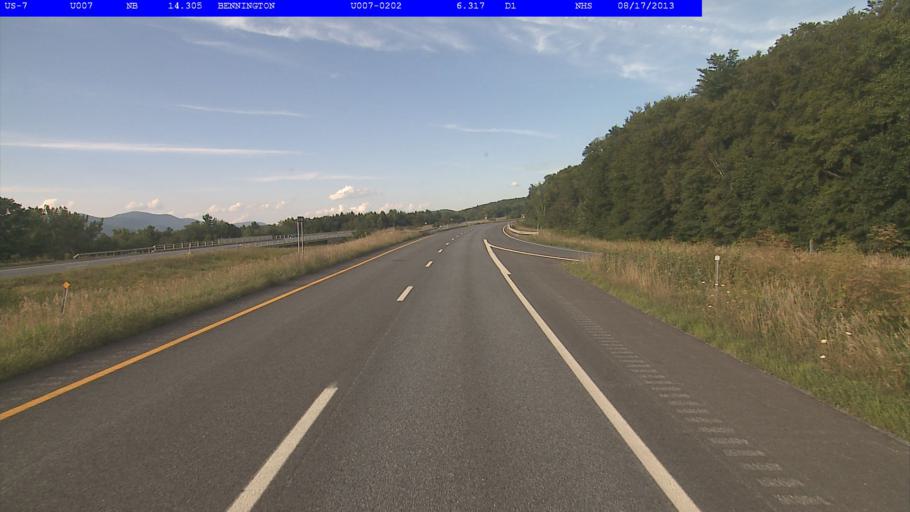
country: US
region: Vermont
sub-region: Bennington County
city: North Bennington
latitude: 42.9219
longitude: -73.2059
